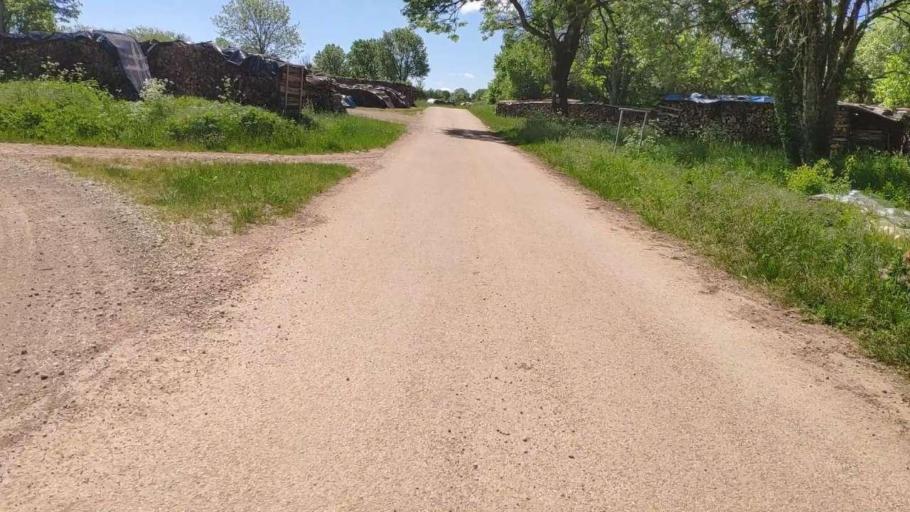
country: FR
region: Franche-Comte
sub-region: Departement du Jura
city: Poligny
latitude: 46.7319
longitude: 5.6965
